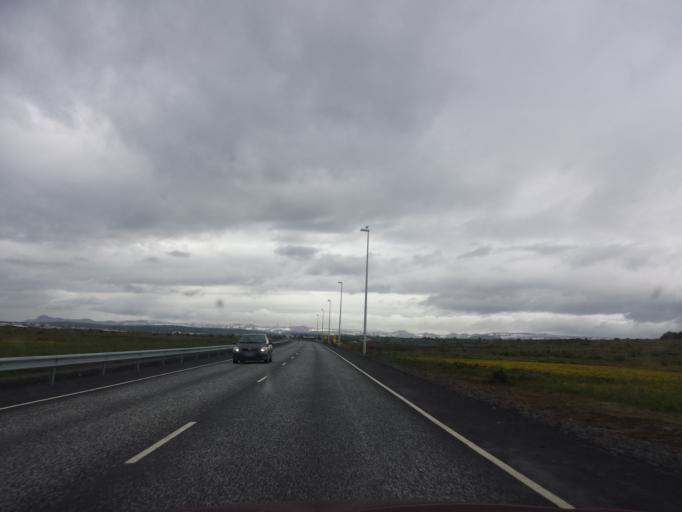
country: IS
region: Capital Region
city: Alftanes
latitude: 64.0937
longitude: -21.9941
